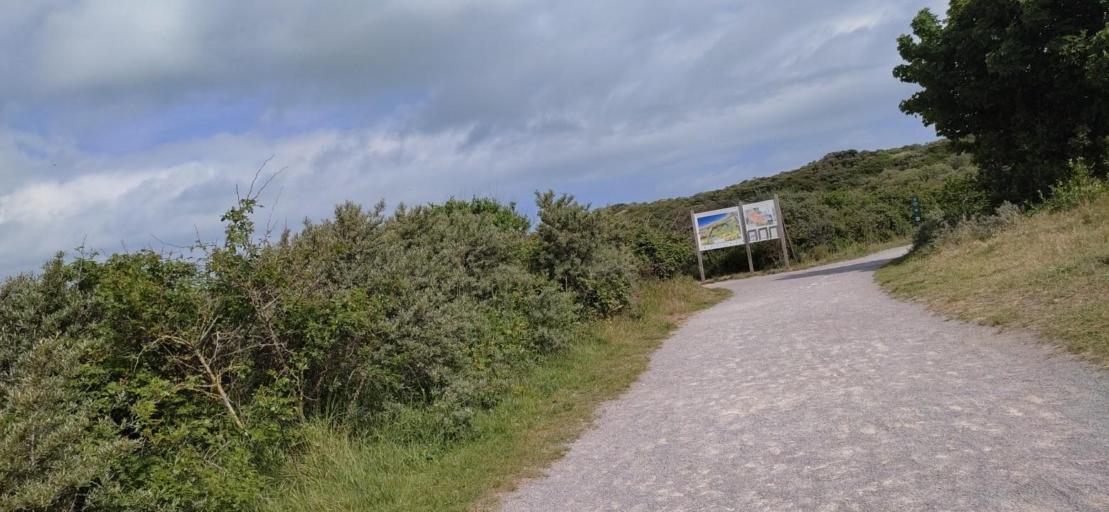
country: FR
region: Nord-Pas-de-Calais
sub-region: Departement du Pas-de-Calais
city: Oye-Plage
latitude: 51.0047
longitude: 2.0665
